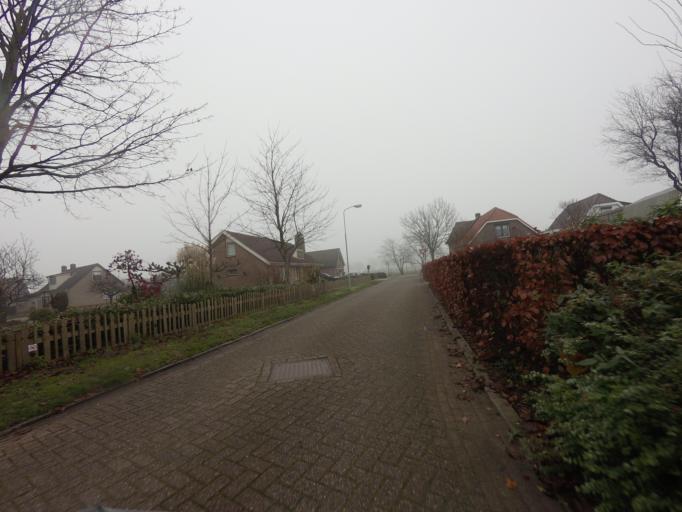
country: NL
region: Gelderland
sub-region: Gemeente Zaltbommel
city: Nederhemert
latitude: 51.7667
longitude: 5.1675
